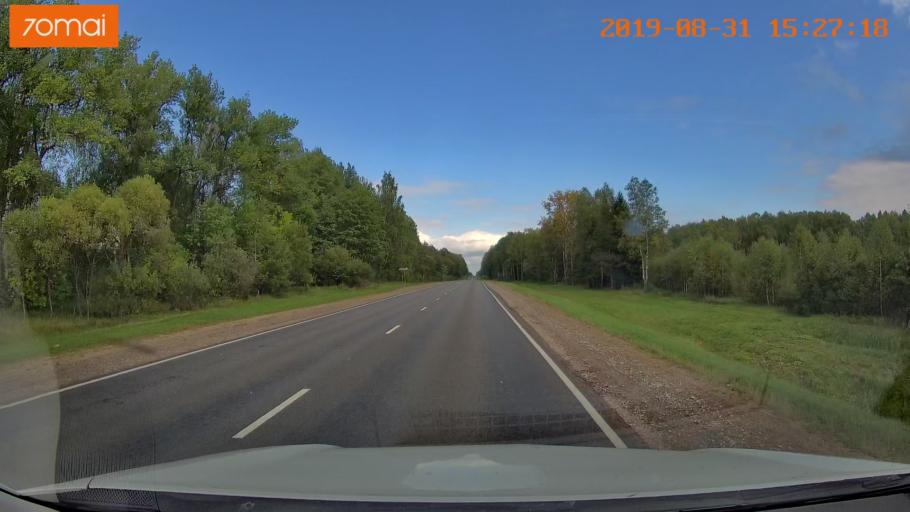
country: RU
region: Kaluga
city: Baryatino
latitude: 54.5547
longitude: 34.5546
